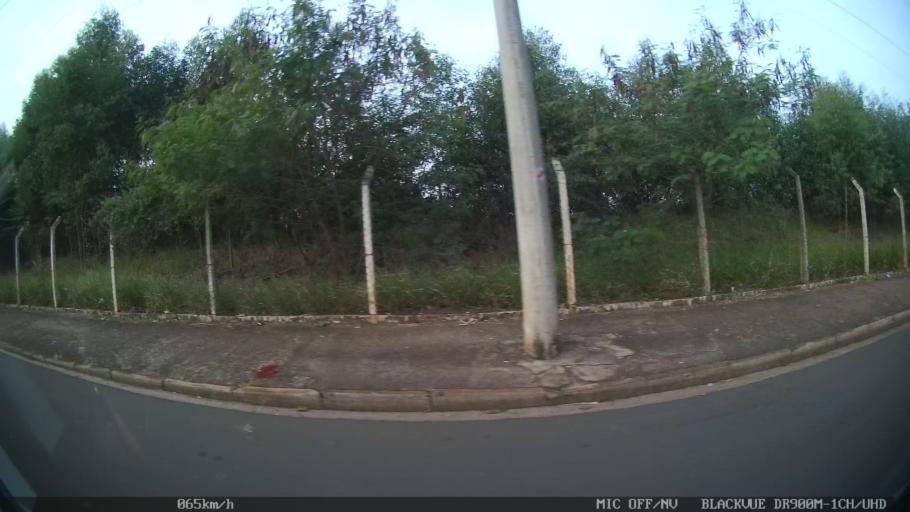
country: BR
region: Sao Paulo
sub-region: Limeira
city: Limeira
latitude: -22.5516
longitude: -47.4267
